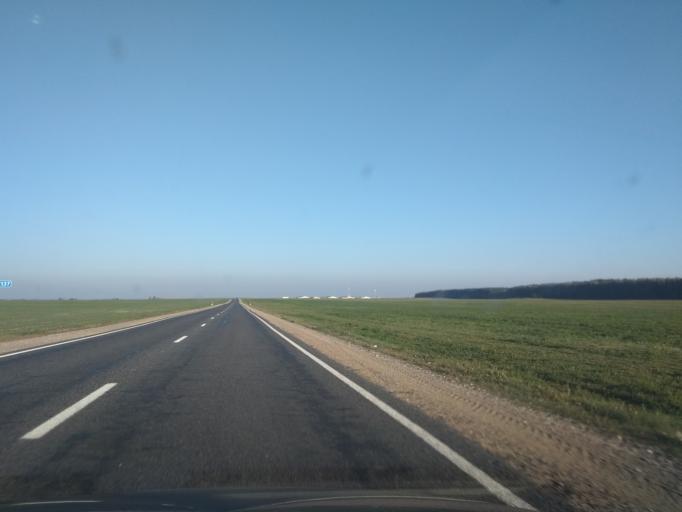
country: BY
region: Grodnenskaya
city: Svislach
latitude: 53.1294
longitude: 24.1545
